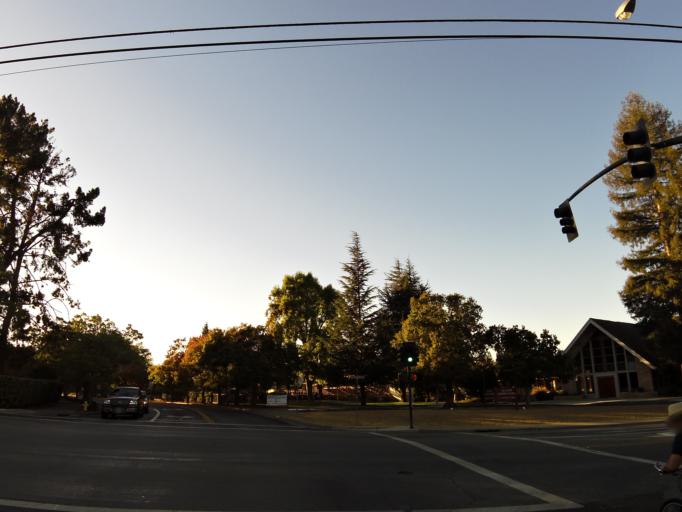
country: US
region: California
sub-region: Santa Clara County
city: Los Altos
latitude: 37.3740
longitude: -122.1074
